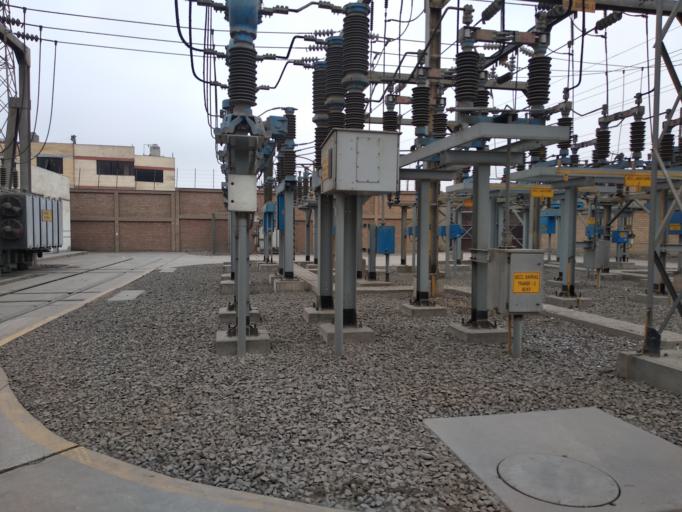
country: PE
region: Lima
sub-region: Lima
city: Urb. Santo Domingo
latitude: -11.8913
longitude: -77.0422
